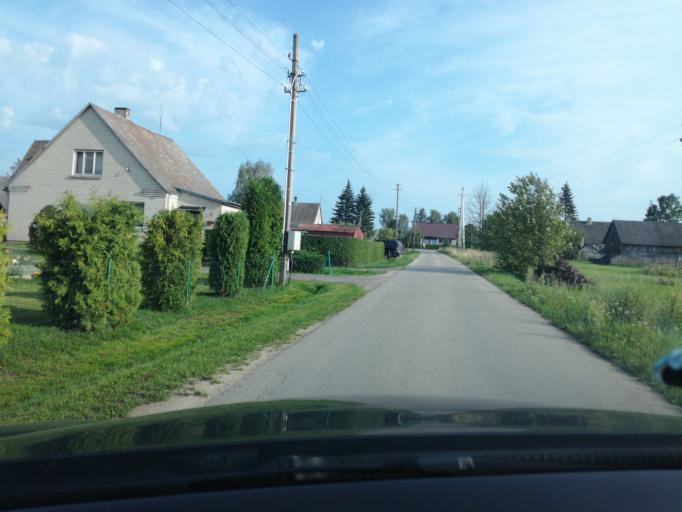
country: LT
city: Simnas
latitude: 54.3854
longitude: 23.6844
